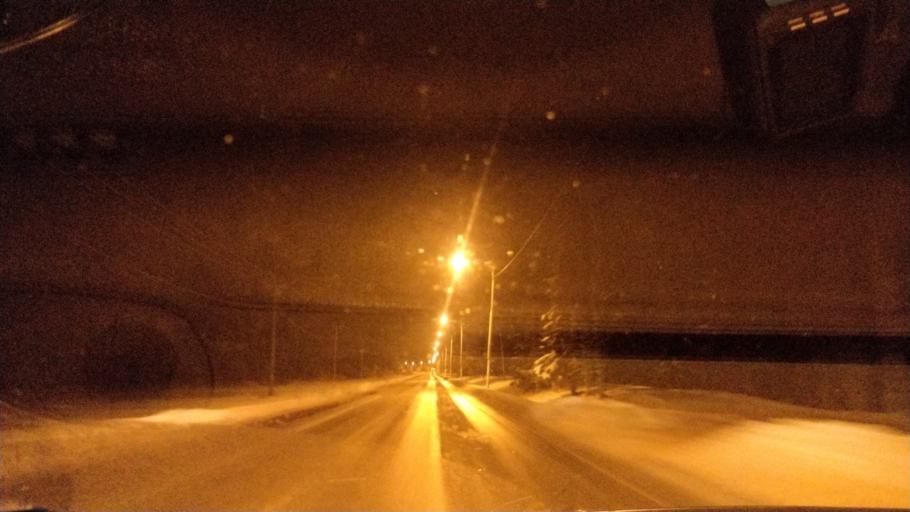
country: FI
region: Lapland
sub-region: Rovaniemi
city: Rovaniemi
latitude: 66.3074
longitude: 25.3594
